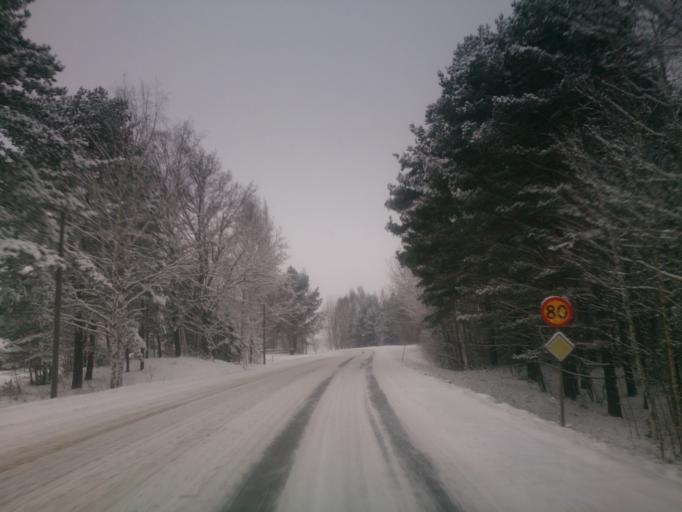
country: SE
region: OEstergoetland
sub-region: Finspangs Kommun
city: Finspang
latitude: 58.6678
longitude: 15.7622
